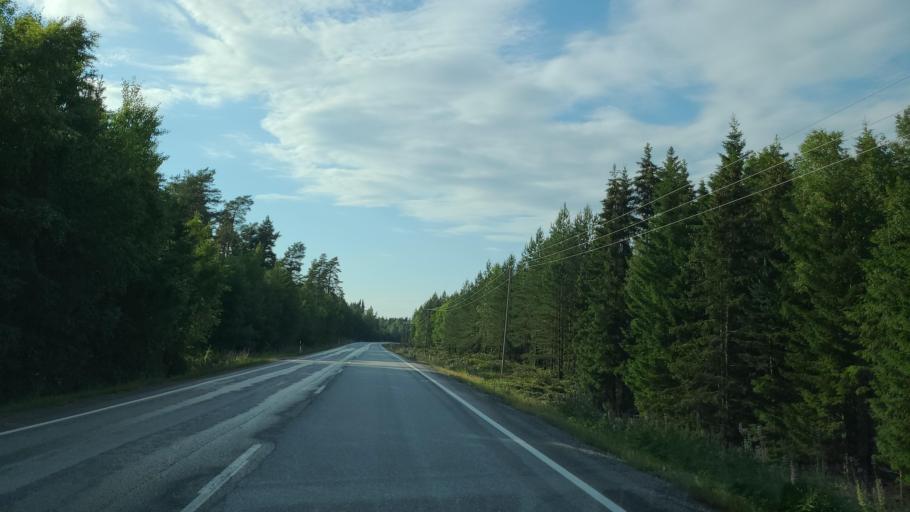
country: FI
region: Ostrobothnia
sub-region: Vaasa
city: Vaasa
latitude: 63.1698
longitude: 21.5846
